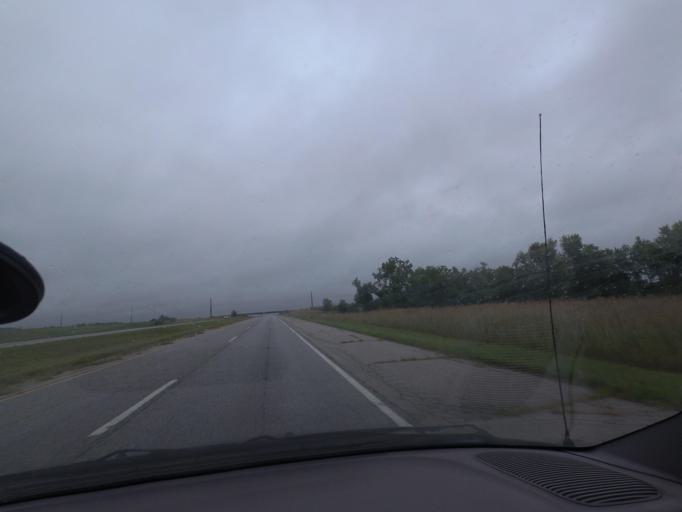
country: US
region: Illinois
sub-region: Pike County
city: Pittsfield
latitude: 39.6709
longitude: -90.8055
